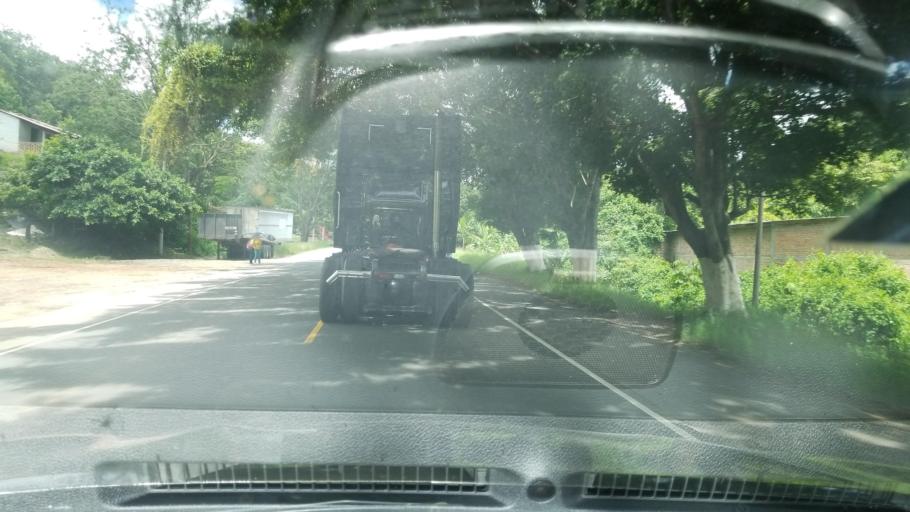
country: HN
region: Francisco Morazan
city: Talanga
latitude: 14.3852
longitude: -87.1348
